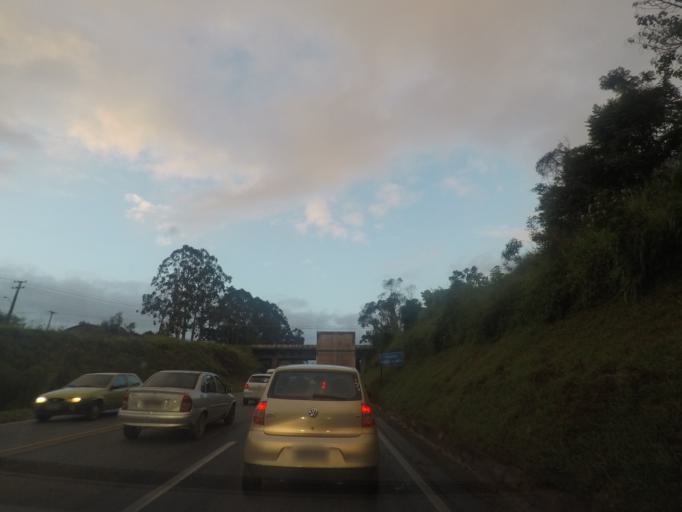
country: BR
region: Parana
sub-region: Curitiba
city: Curitiba
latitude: -25.4086
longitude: -49.3647
